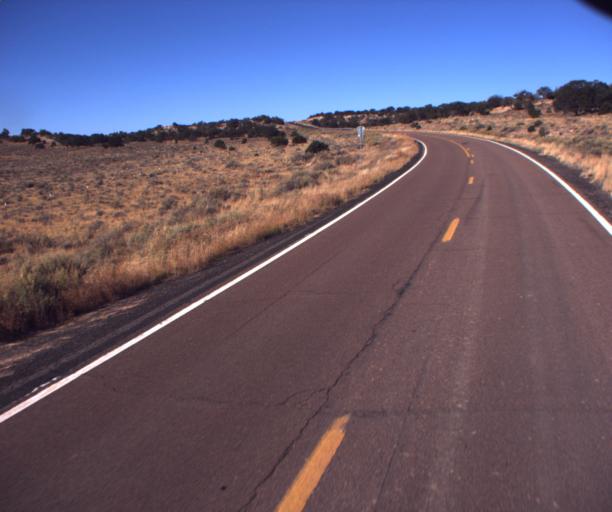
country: US
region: Arizona
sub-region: Navajo County
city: First Mesa
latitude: 35.7668
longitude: -109.9869
